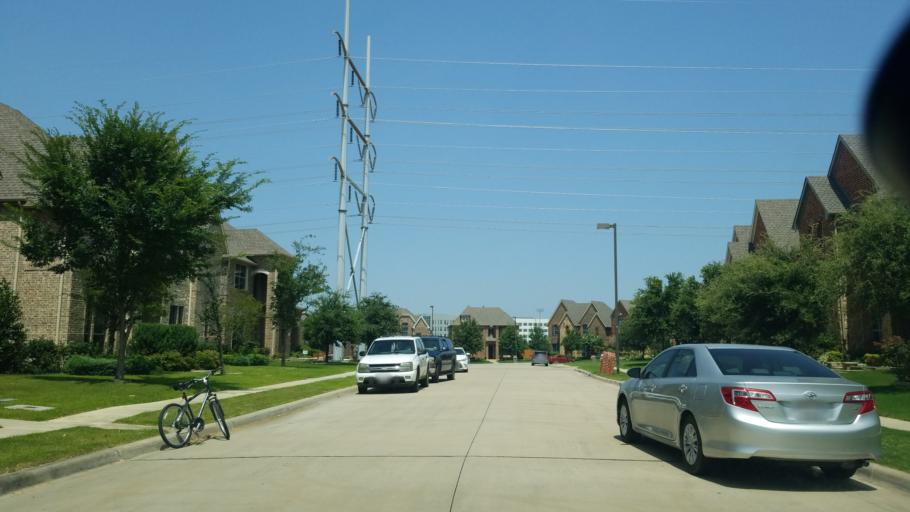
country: US
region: Texas
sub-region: Dallas County
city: Coppell
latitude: 32.9245
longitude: -96.9801
